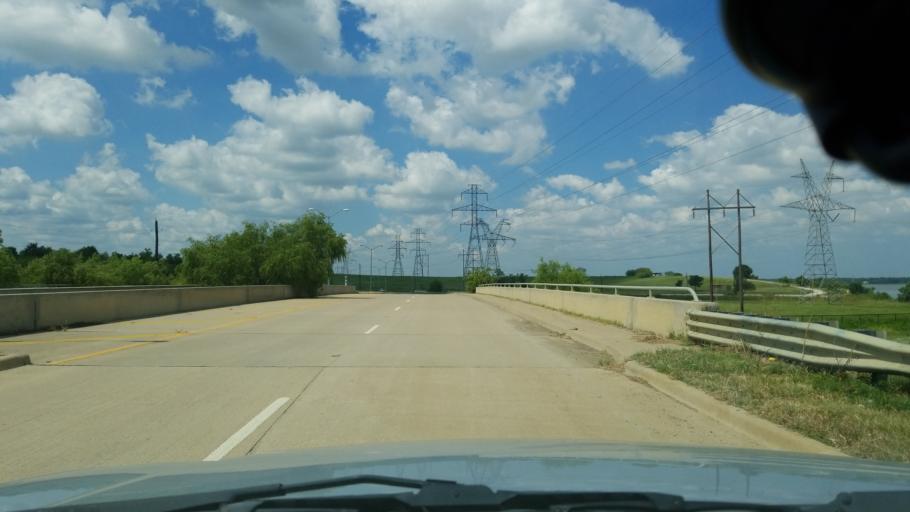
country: US
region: Texas
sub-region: Dallas County
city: Grand Prairie
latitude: 32.7164
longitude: -96.9498
